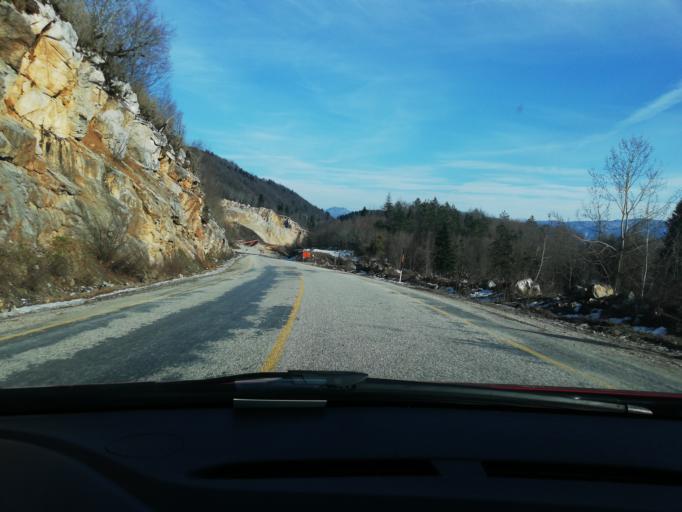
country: TR
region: Kastamonu
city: Senpazar
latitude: 41.8118
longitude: 33.1099
